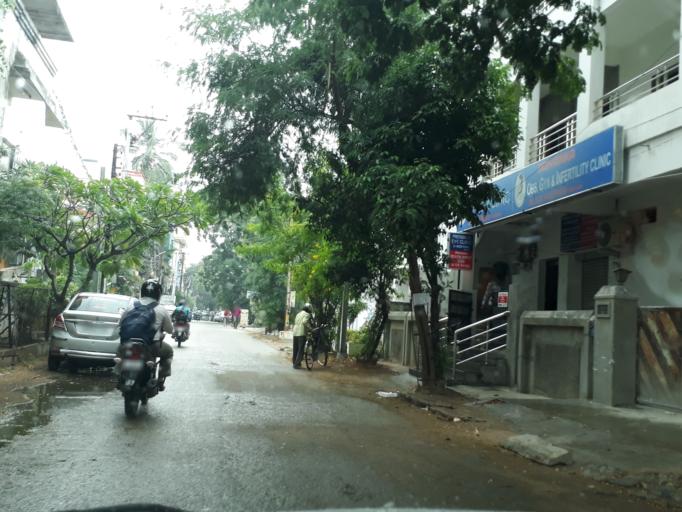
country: IN
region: Telangana
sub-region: Hyderabad
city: Malkajgiri
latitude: 17.4619
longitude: 78.5015
